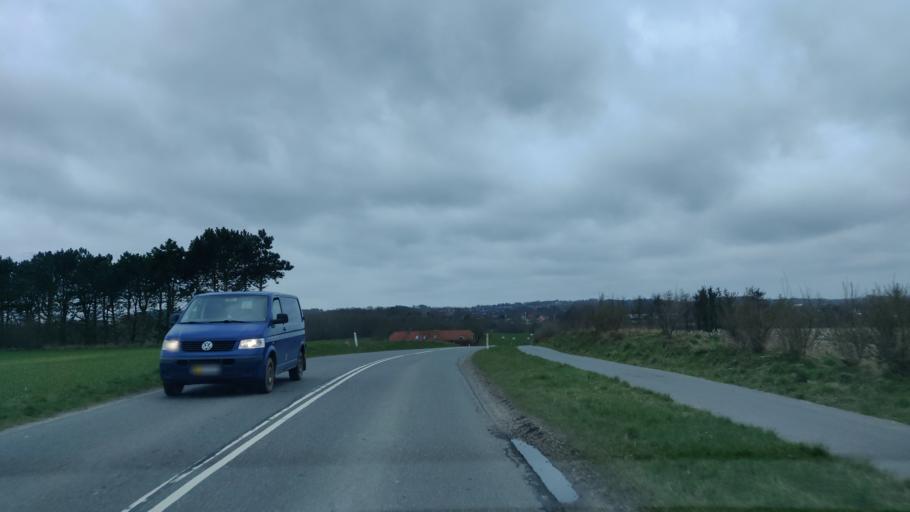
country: DK
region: Central Jutland
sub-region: Viborg Kommune
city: Stoholm
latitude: 56.4873
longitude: 9.1671
